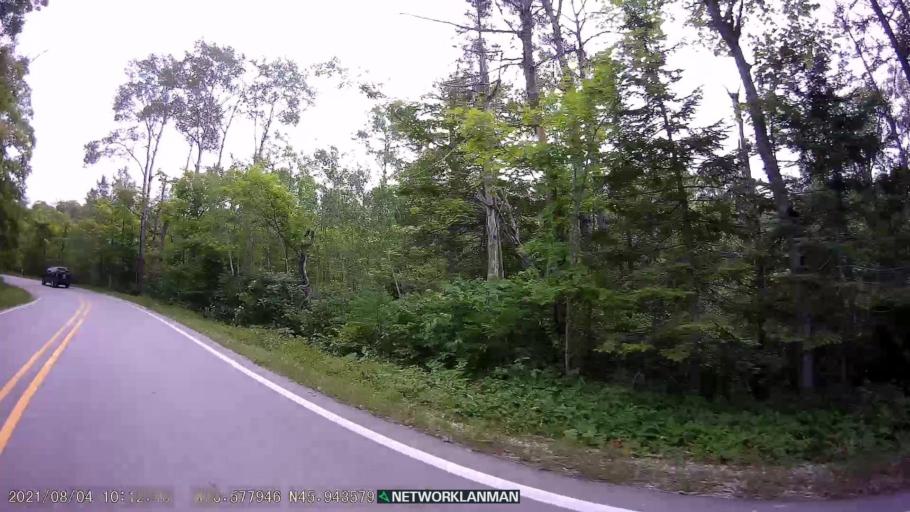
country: CA
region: Ontario
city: Thessalon
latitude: 45.9436
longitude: -83.5779
